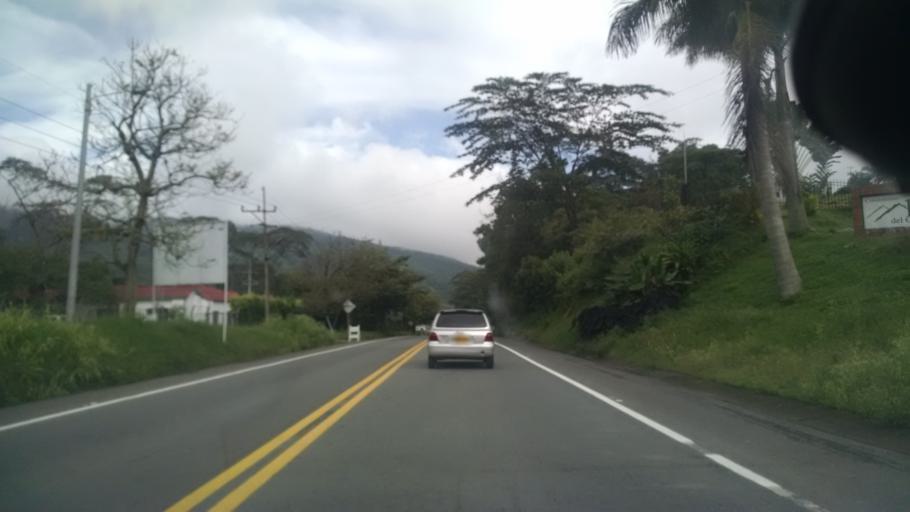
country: CO
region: Caldas
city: Palestina
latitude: 5.0273
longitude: -75.5972
